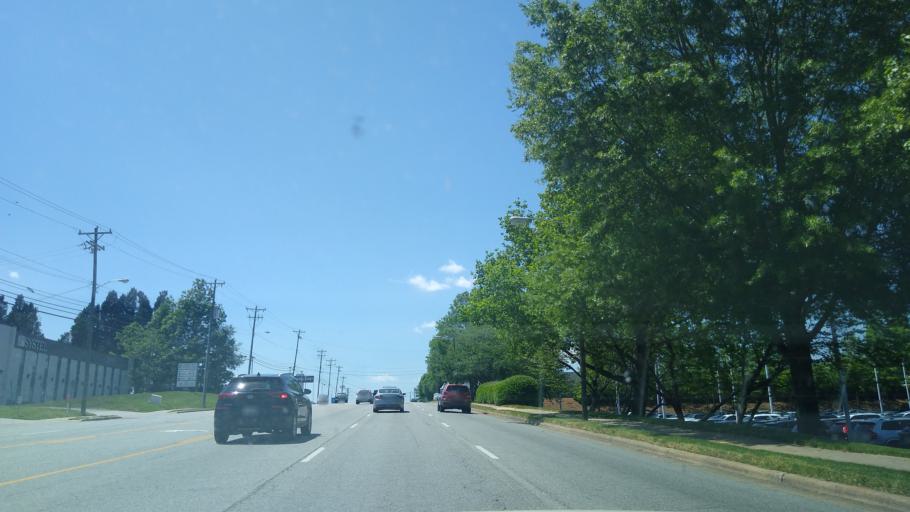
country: US
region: North Carolina
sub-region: Guilford County
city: Greensboro
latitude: 36.0603
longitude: -79.8655
